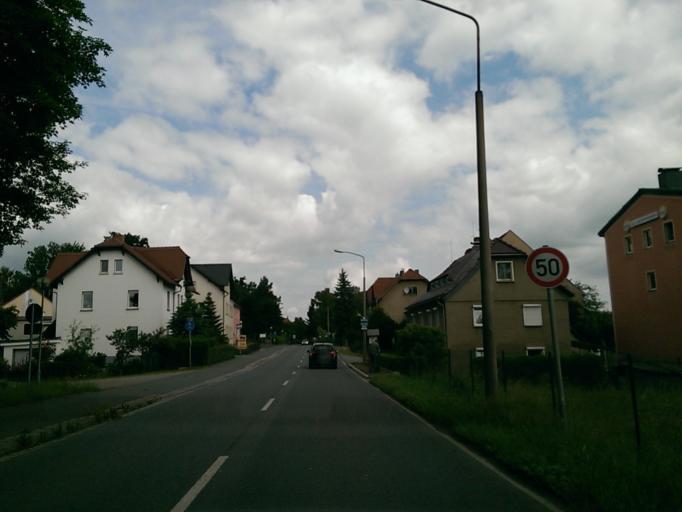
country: DE
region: Saxony
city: Mittelherwigsdorf
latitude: 50.9476
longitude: 14.7368
